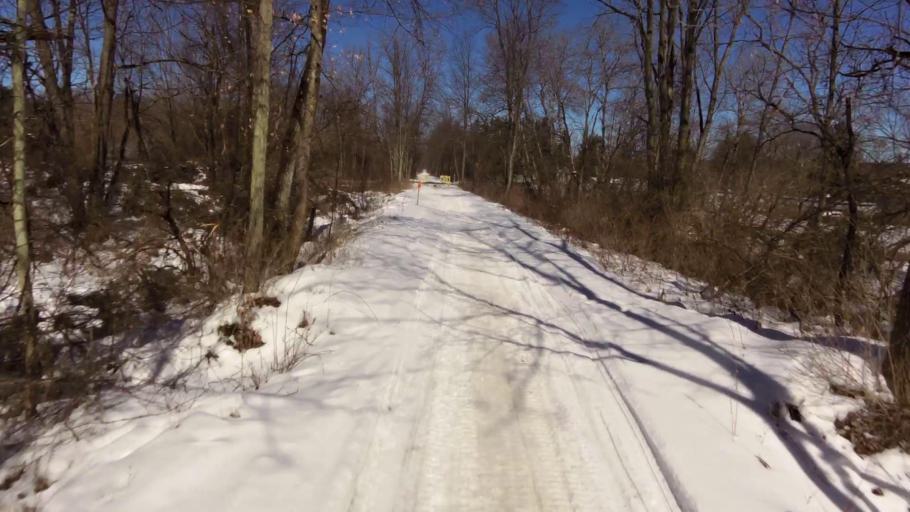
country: US
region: New York
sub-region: Allegany County
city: Houghton
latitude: 42.3644
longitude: -78.1366
